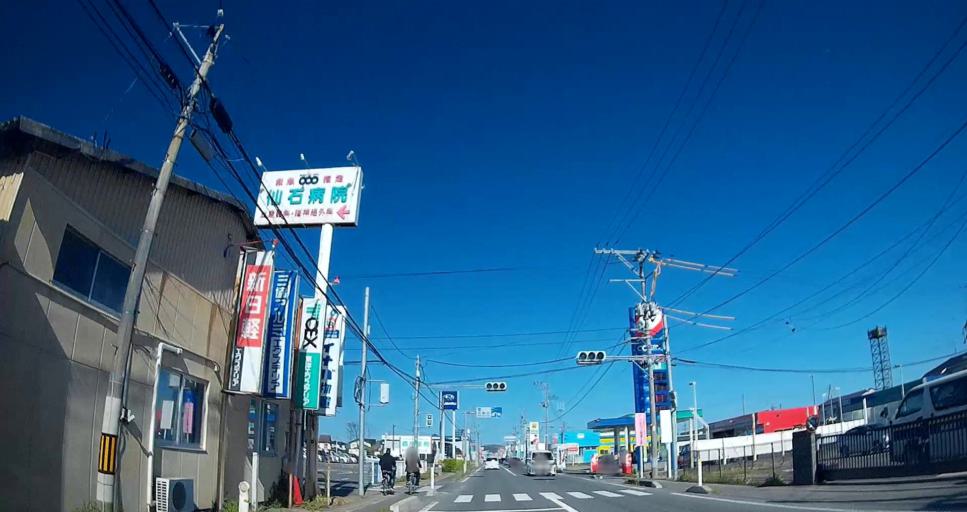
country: JP
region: Miyagi
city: Yamoto
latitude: 38.4309
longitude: 141.2575
